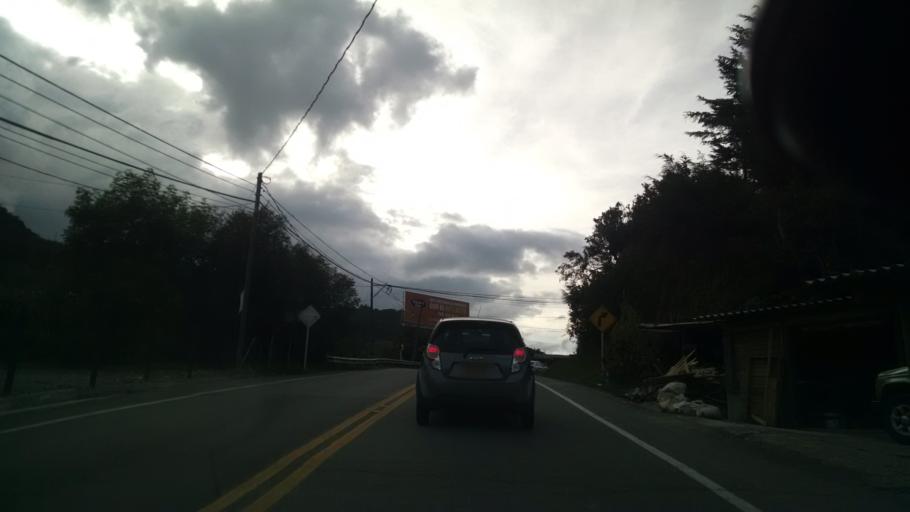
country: CO
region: Antioquia
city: El Retiro
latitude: 6.1352
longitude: -75.5092
